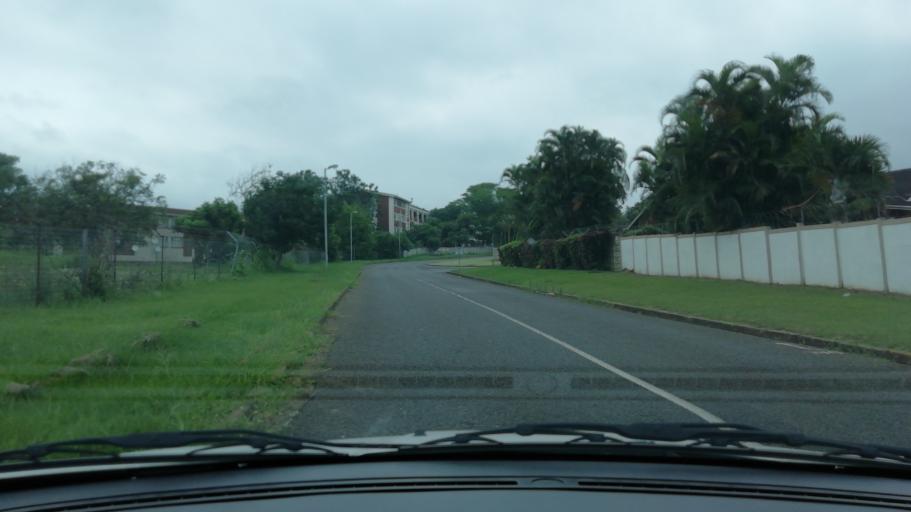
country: ZA
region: KwaZulu-Natal
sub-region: uThungulu District Municipality
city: Empangeni
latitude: -28.7396
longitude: 31.9010
